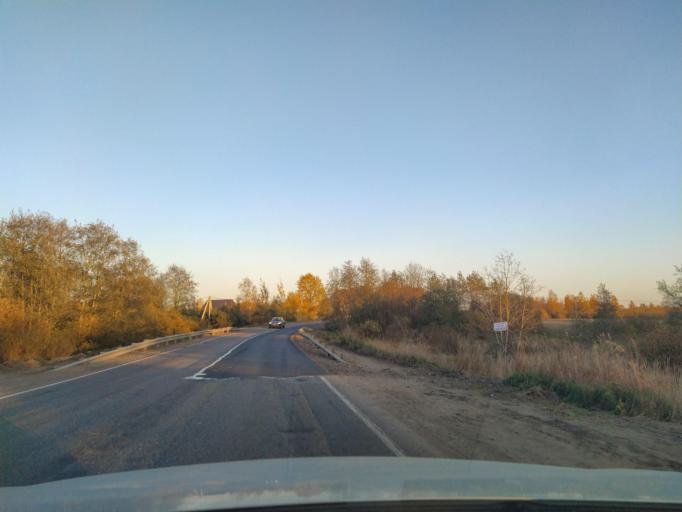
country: RU
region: Leningrad
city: Maloye Verevo
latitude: 59.6161
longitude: 30.2143
